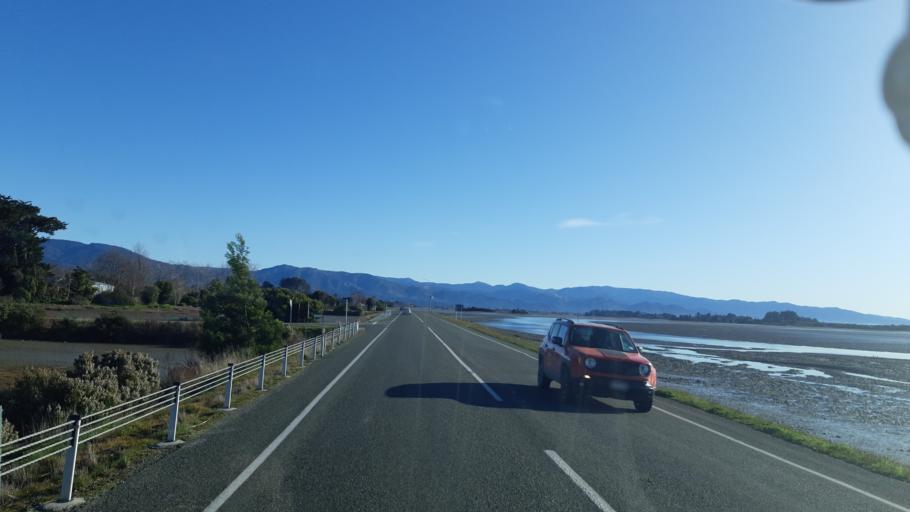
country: NZ
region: Tasman
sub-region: Tasman District
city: Motueka
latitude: -41.1789
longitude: 173.0433
